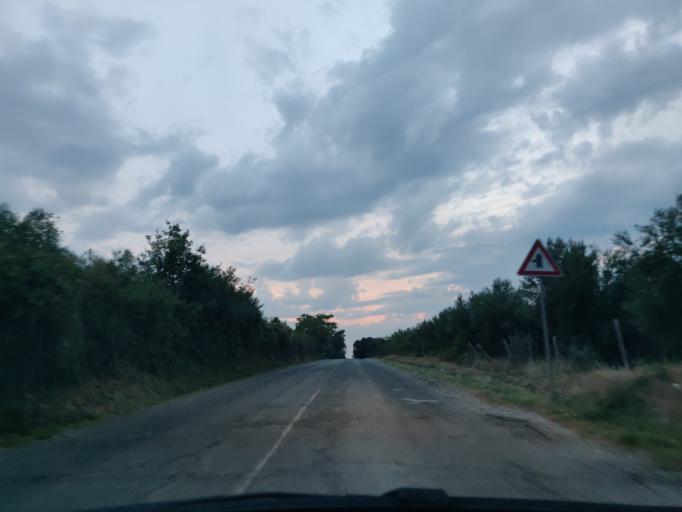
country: IT
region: Latium
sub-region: Provincia di Viterbo
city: San Martino al Cimino
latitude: 42.3784
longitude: 12.0706
